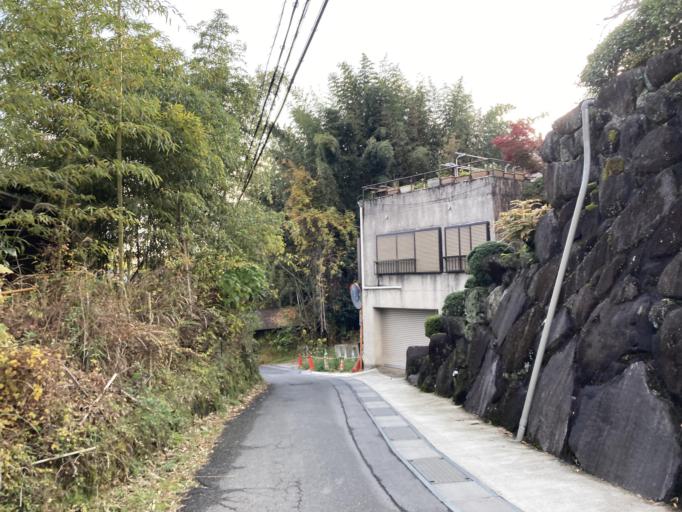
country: JP
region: Nara
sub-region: Ikoma-shi
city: Ikoma
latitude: 34.6741
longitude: 135.6898
